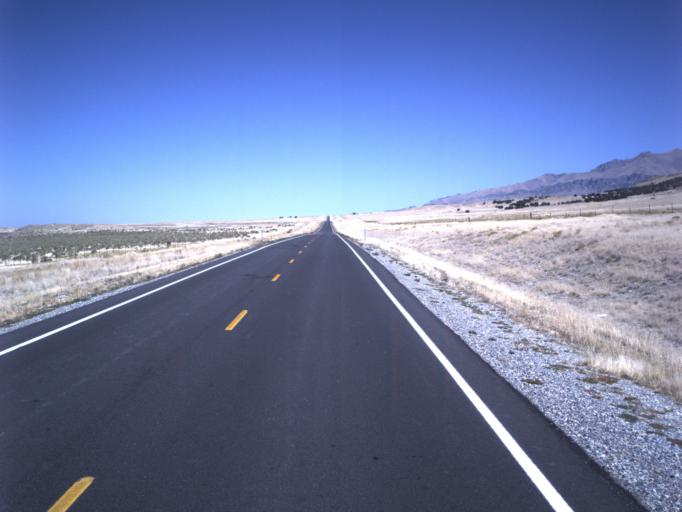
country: US
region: Utah
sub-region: Tooele County
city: Grantsville
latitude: 40.5585
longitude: -112.7365
